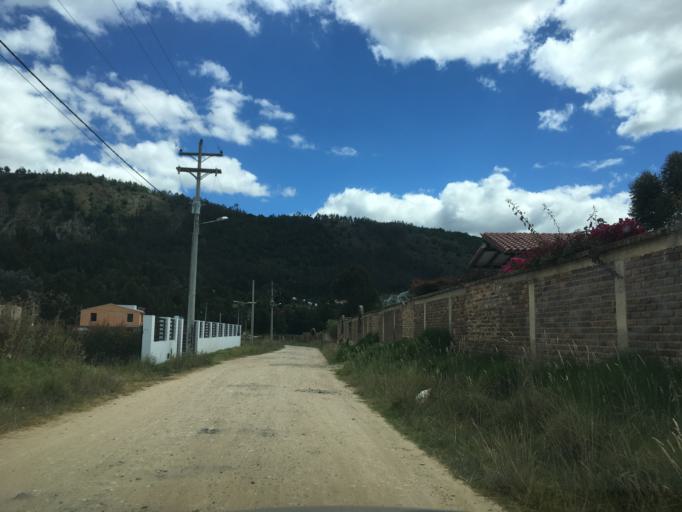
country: CO
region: Boyaca
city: Firavitoba
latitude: 5.6741
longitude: -72.9582
